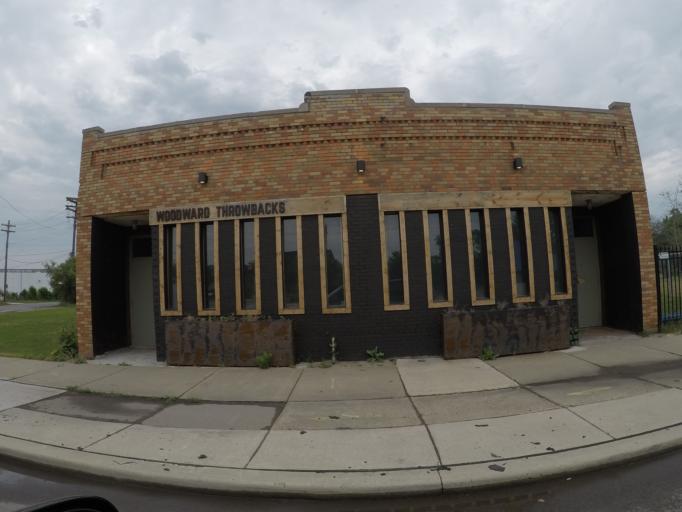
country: US
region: Michigan
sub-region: Wayne County
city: Detroit
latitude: 42.3314
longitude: -83.0923
